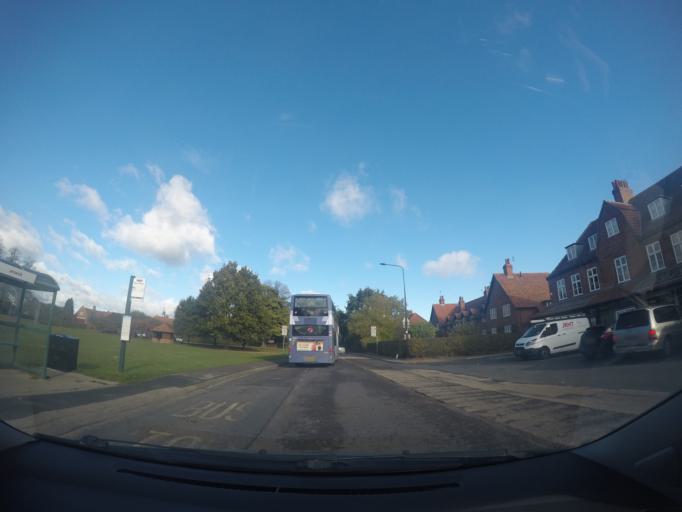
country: GB
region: England
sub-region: City of York
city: Haxby
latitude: 53.9913
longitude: -1.0727
